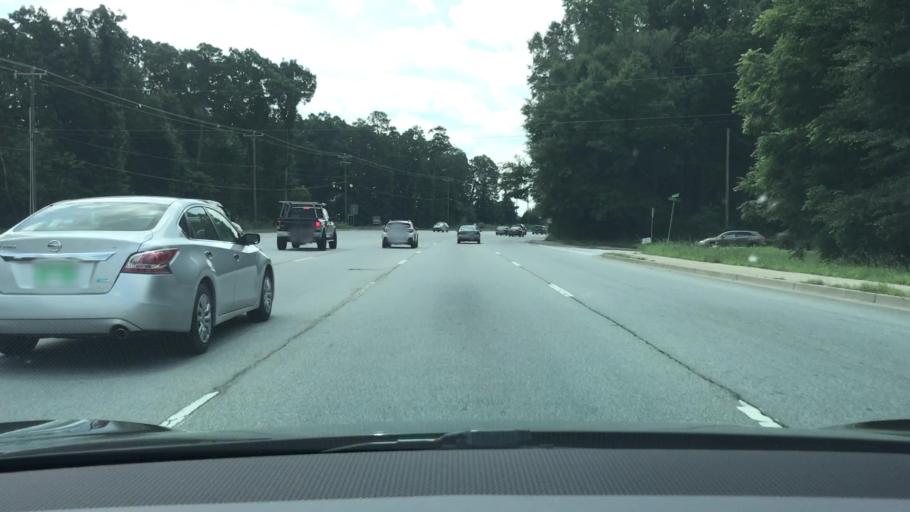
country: US
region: South Carolina
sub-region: Greenville County
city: Berea
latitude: 34.9137
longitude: -82.4615
